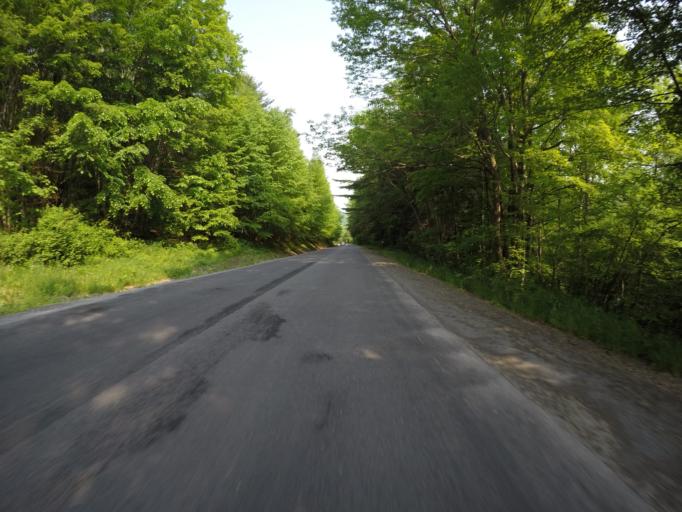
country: US
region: New York
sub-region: Sullivan County
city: Livingston Manor
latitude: 42.1208
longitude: -74.6856
